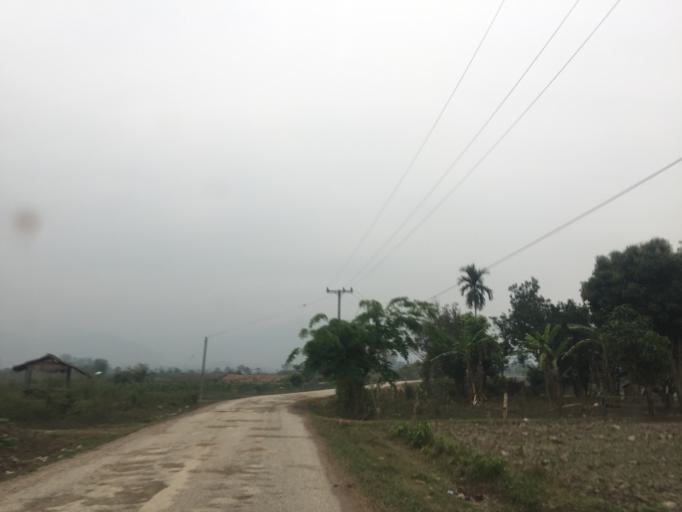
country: LA
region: Xiagnabouli
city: Sainyabuli
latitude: 18.9806
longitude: 101.4988
